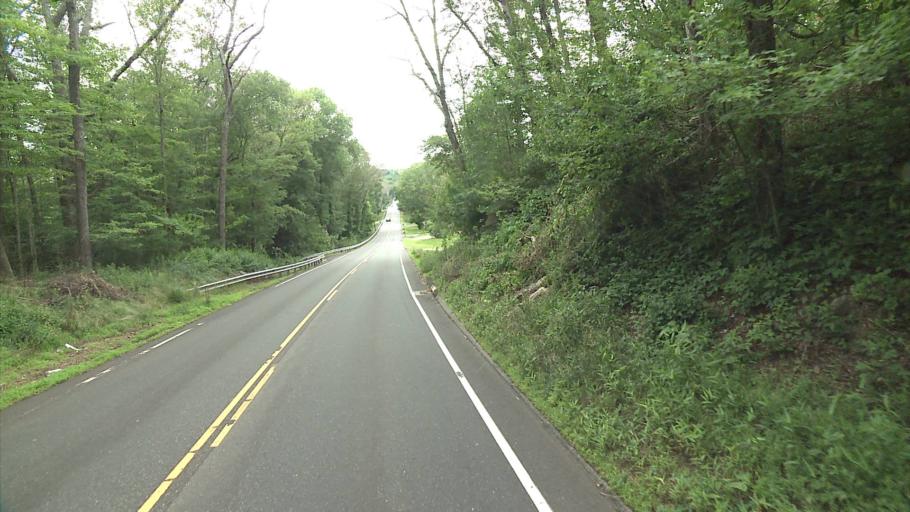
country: US
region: Connecticut
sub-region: New London County
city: Ledyard Center
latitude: 41.4639
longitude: -72.0199
